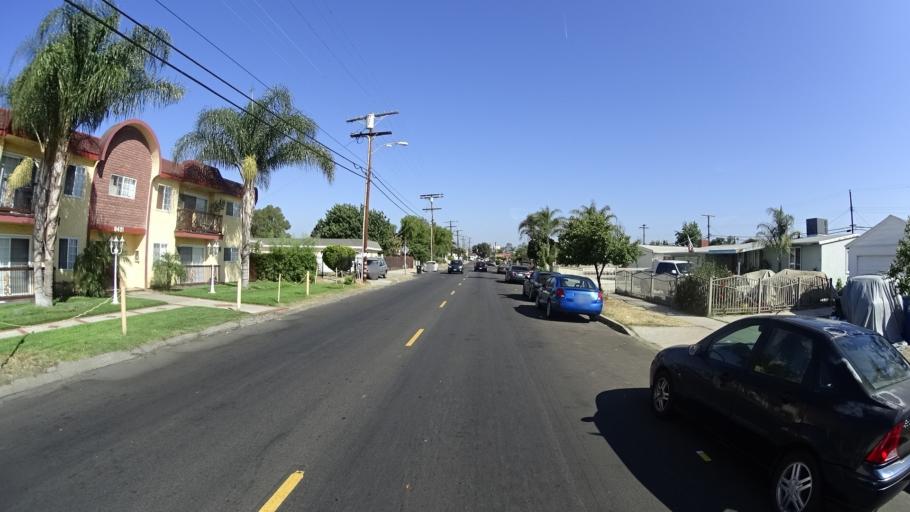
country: US
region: California
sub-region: Los Angeles County
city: Van Nuys
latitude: 34.2244
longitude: -118.4306
